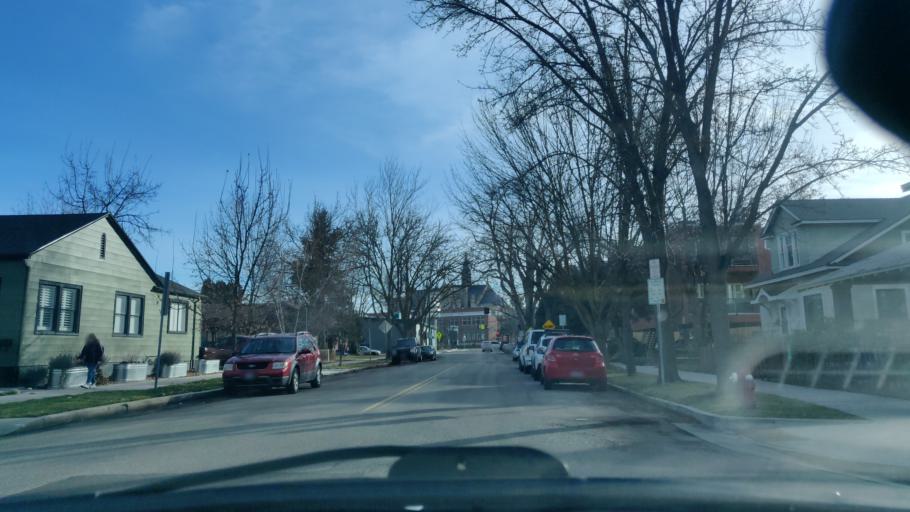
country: US
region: Idaho
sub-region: Ada County
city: Boise
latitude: 43.6240
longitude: -116.1987
